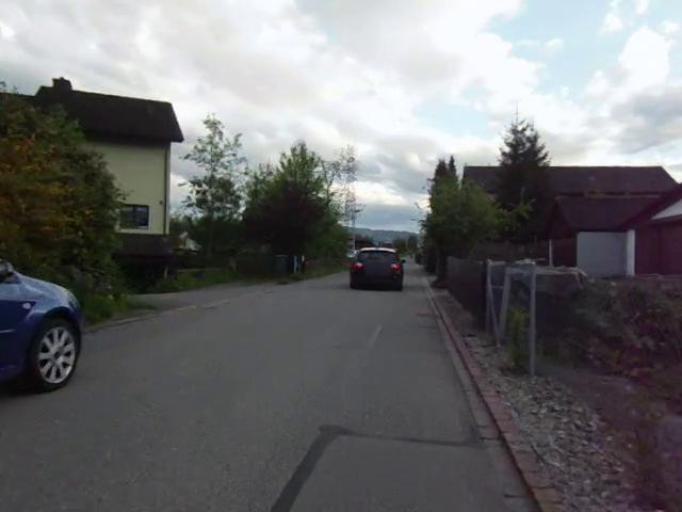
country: CH
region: Zurich
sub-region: Bezirk Hinwil
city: Rueti / Westlicher Dorfteil
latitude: 47.2511
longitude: 8.8436
